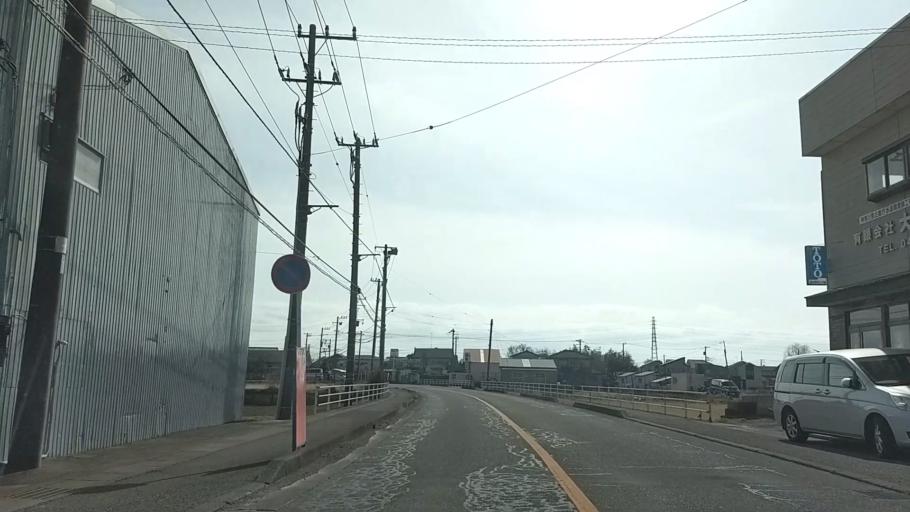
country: JP
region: Kanagawa
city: Chigasaki
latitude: 35.3574
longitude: 139.3843
